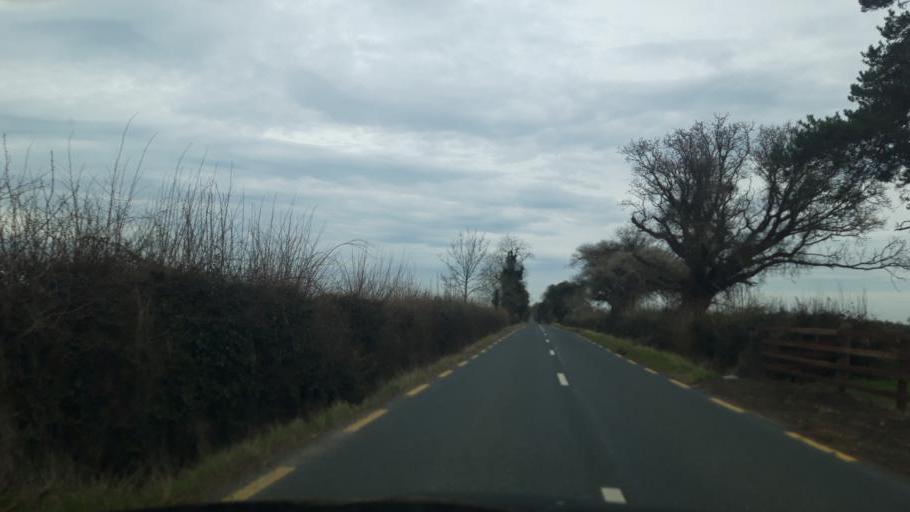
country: IE
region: Leinster
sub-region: Kildare
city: Clane
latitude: 53.3135
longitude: -6.7134
